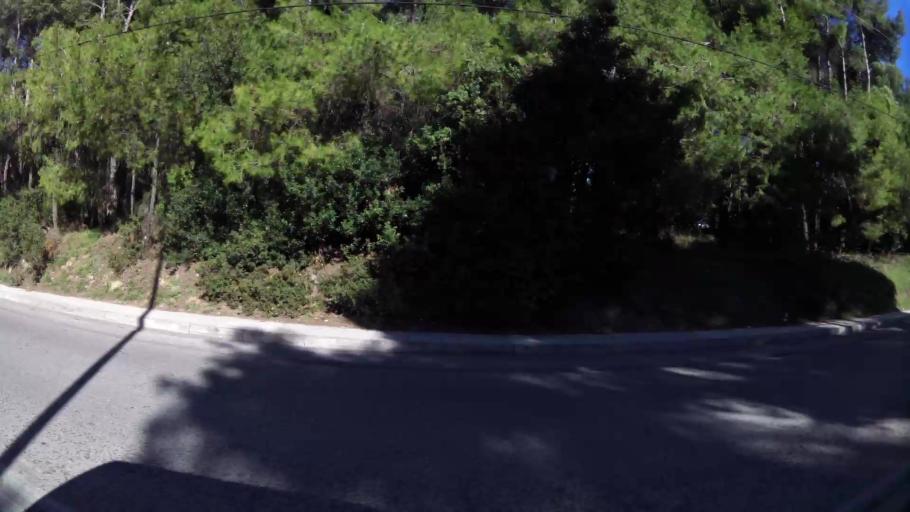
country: GR
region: Attica
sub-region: Nomarchia Anatolikis Attikis
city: Drosia
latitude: 38.1232
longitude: 23.8570
